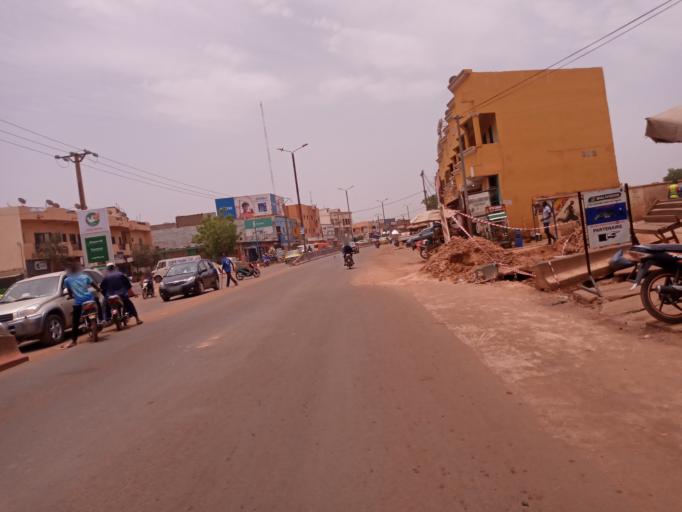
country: ML
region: Bamako
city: Bamako
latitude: 12.5990
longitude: -8.0134
